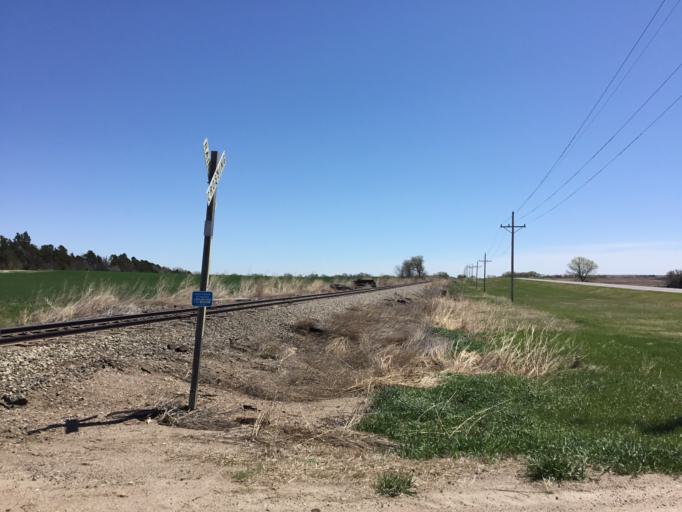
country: US
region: Kansas
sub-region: Phillips County
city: Phillipsburg
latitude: 39.8133
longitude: -99.5154
